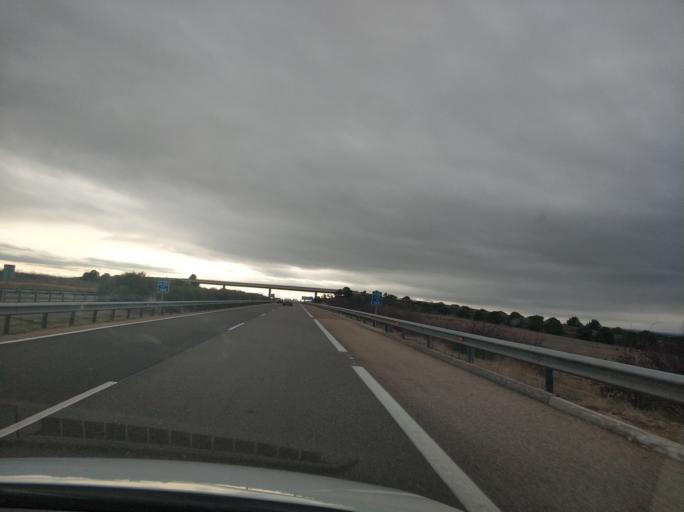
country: ES
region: Castille and Leon
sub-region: Provincia de Valladolid
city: Pollos
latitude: 41.4178
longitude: -5.1223
